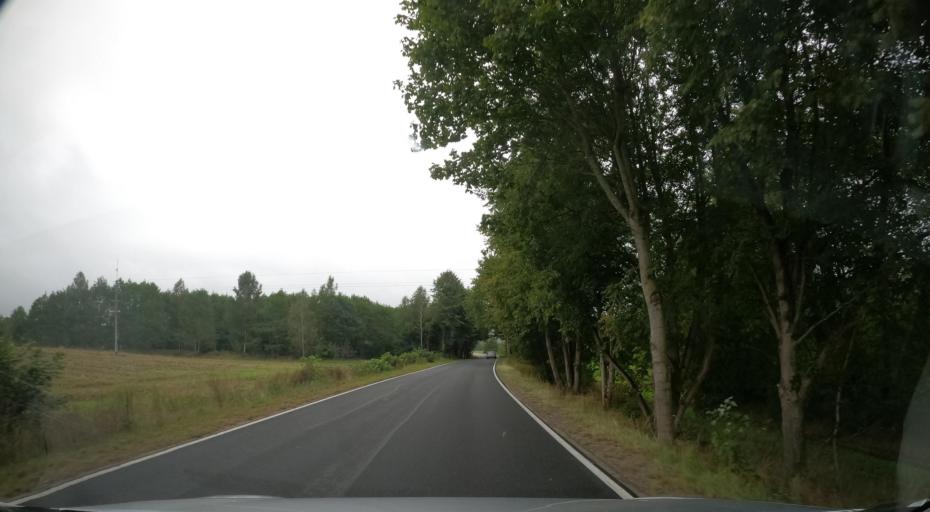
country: PL
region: Pomeranian Voivodeship
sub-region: Powiat wejherowski
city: Linia
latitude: 54.4698
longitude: 17.8547
